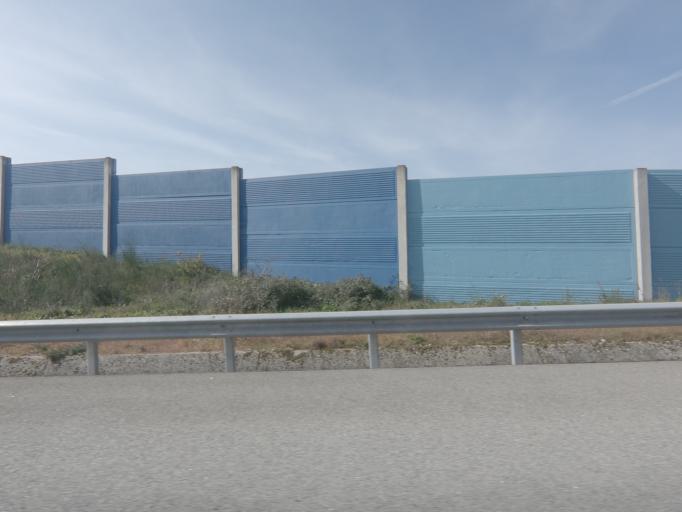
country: PT
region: Viseu
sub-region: Vouzela
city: Vouzela
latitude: 40.6864
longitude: -8.1416
